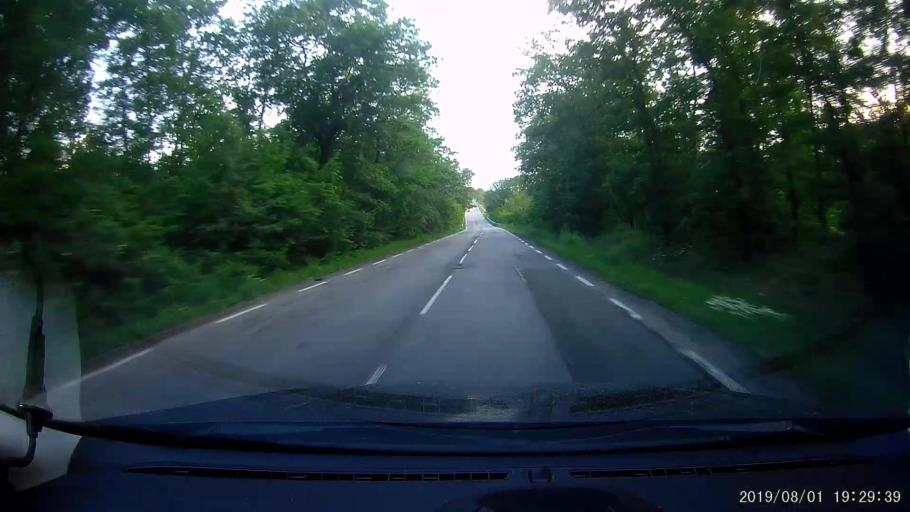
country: BG
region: Burgas
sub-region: Obshtina Sungurlare
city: Sungurlare
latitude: 42.8233
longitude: 26.9045
